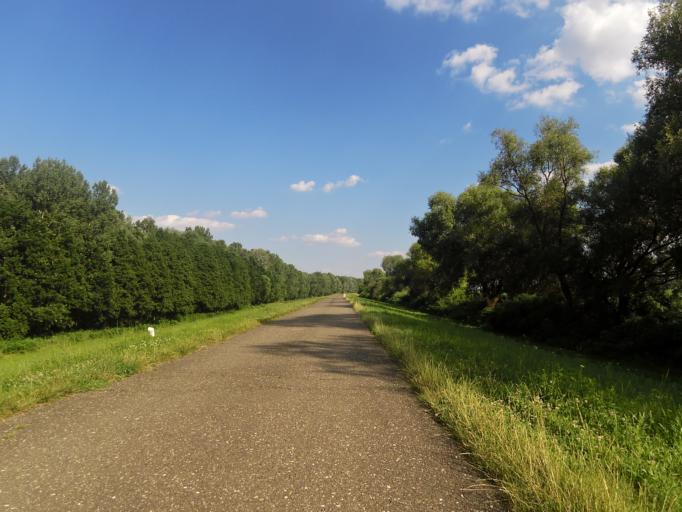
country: HU
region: Jasz-Nagykun-Szolnok
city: Abadszalok
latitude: 47.5090
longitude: 20.5916
